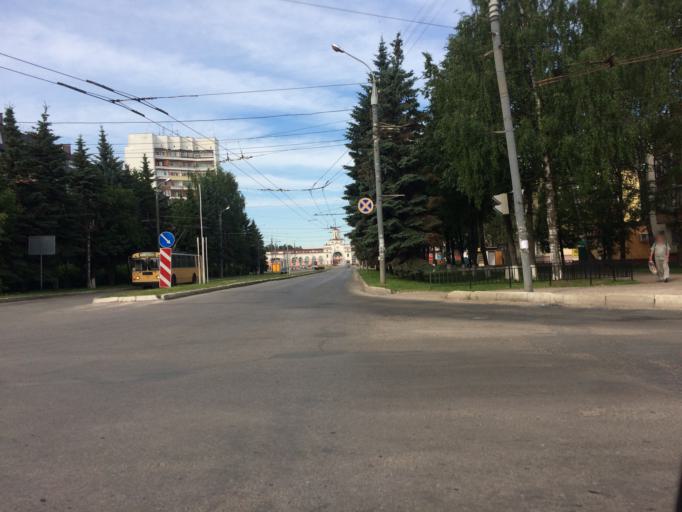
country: RU
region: Mariy-El
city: Yoshkar-Ola
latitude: 56.6235
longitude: 47.8845
